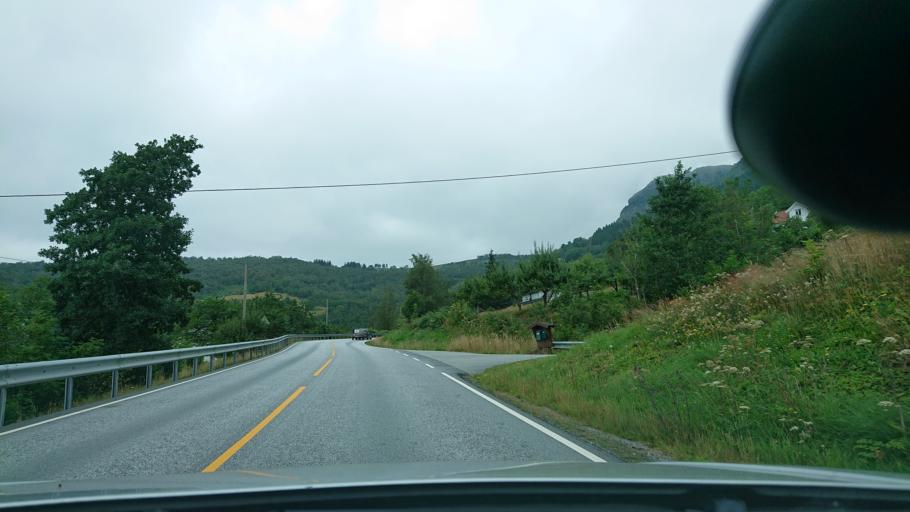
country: NO
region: Rogaland
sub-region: Hjelmeland
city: Hjelmelandsvagen
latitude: 59.1689
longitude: 6.1707
